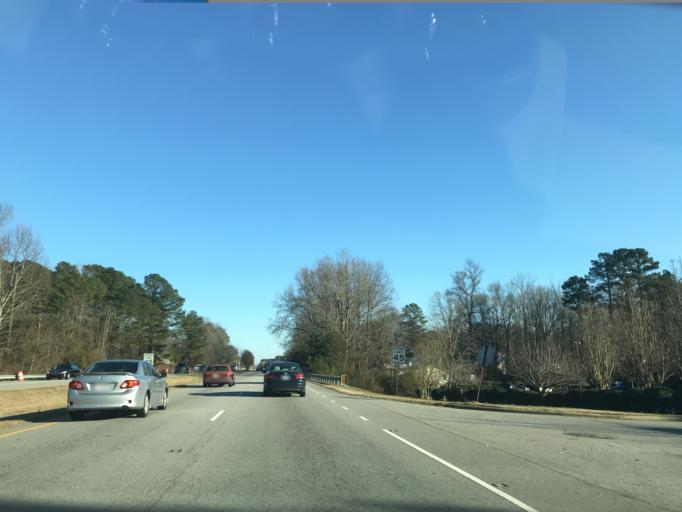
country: US
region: North Carolina
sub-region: Wake County
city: Garner
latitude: 35.7041
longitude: -78.6073
